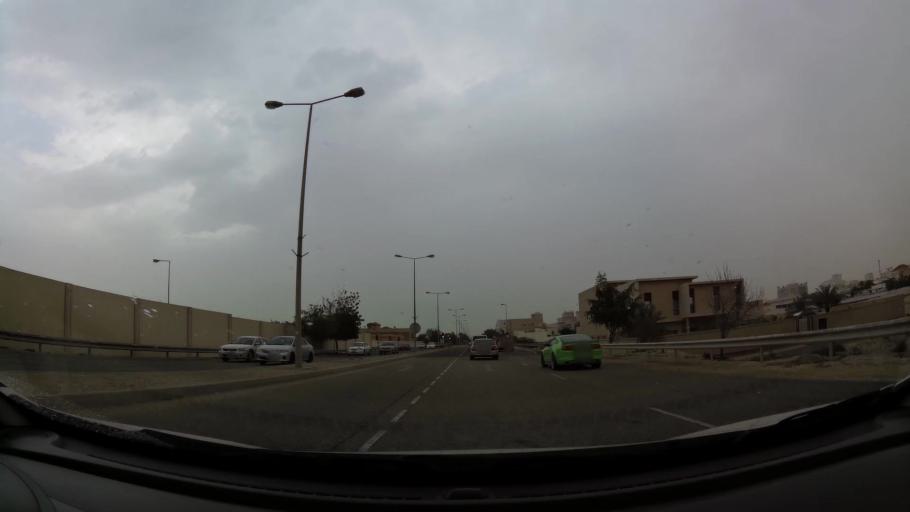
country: BH
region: Northern
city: Ar Rifa'
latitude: 26.1405
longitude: 50.5536
